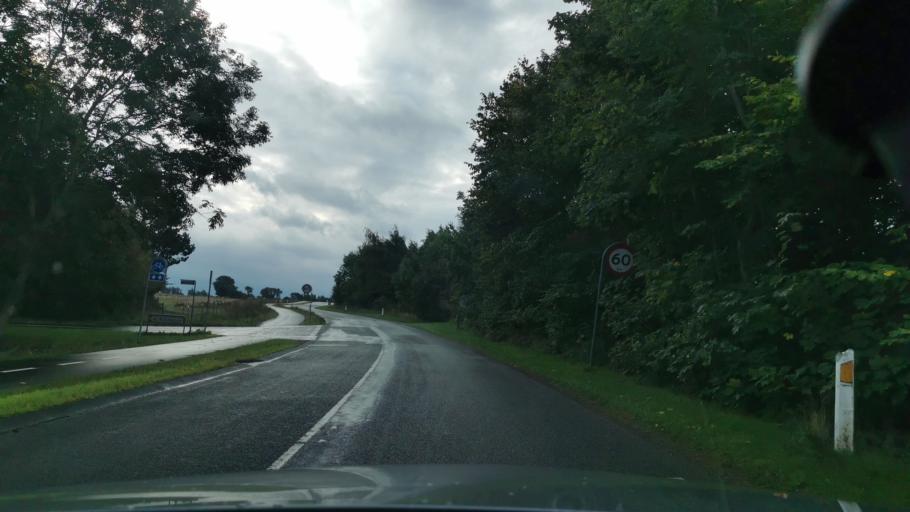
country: DK
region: Zealand
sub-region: Kalundborg Kommune
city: Kalundborg
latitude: 55.7244
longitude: 11.0026
